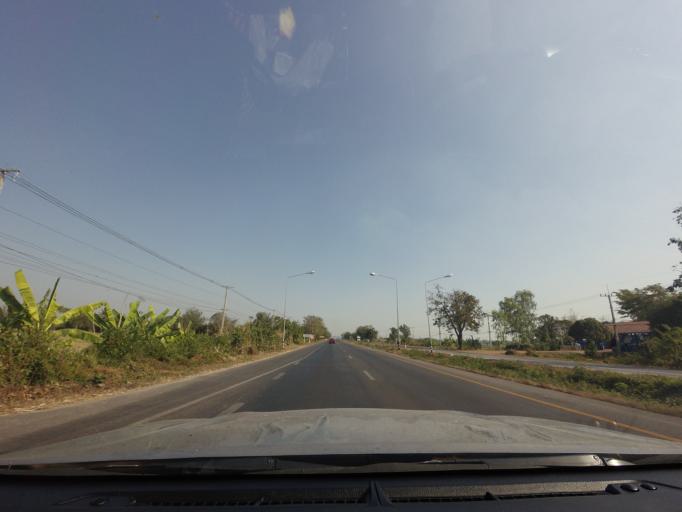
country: TH
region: Kamphaeng Phet
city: Khlong Khlung
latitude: 16.3351
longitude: 99.6192
